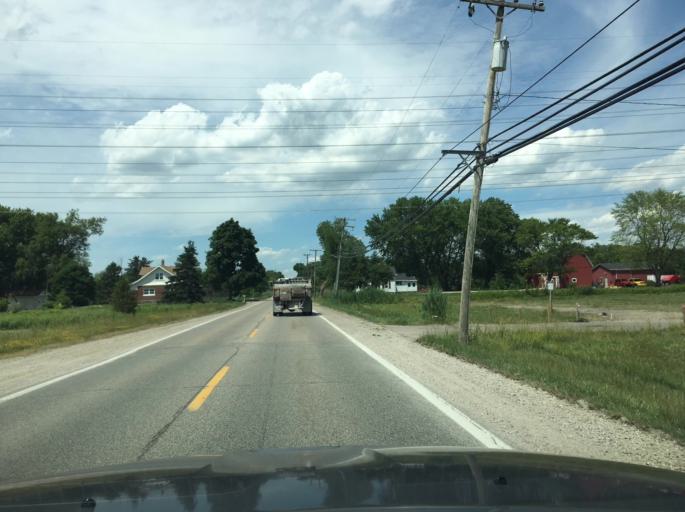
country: US
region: Michigan
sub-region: Macomb County
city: Shelby
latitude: 42.7229
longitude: -82.9598
